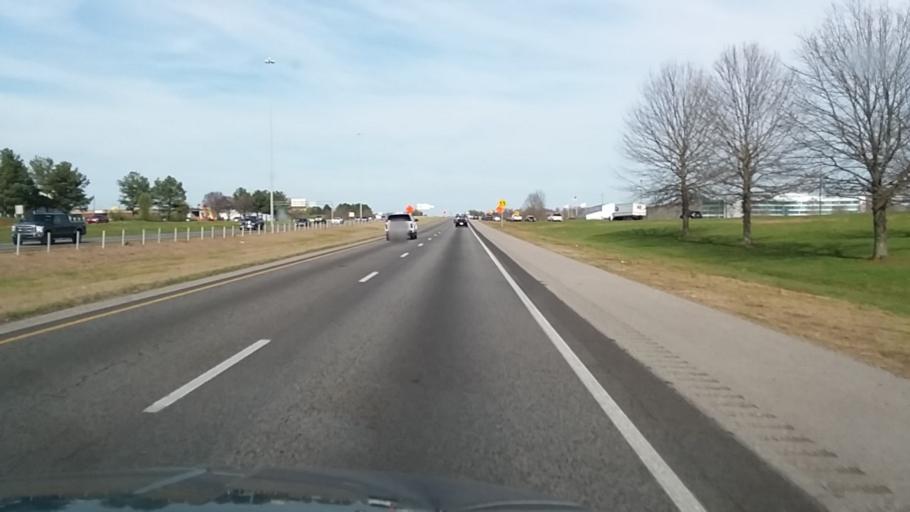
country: US
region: Alabama
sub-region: Madison County
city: Madison
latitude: 34.6737
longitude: -86.7512
